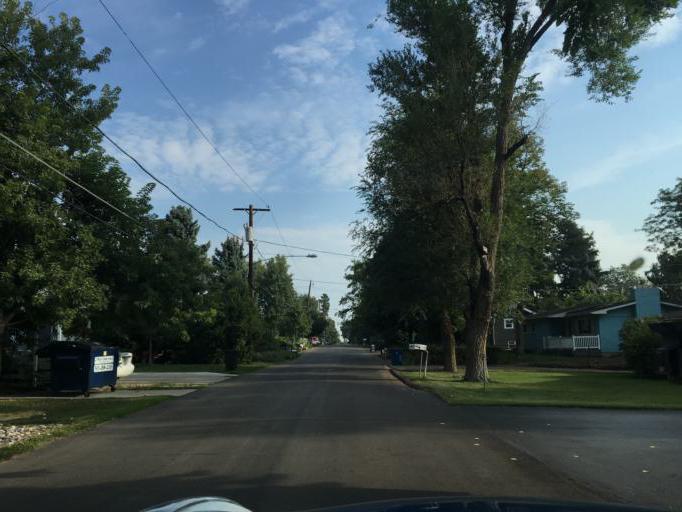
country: US
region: Colorado
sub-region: Jefferson County
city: Wheat Ridge
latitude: 39.7491
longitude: -105.1041
